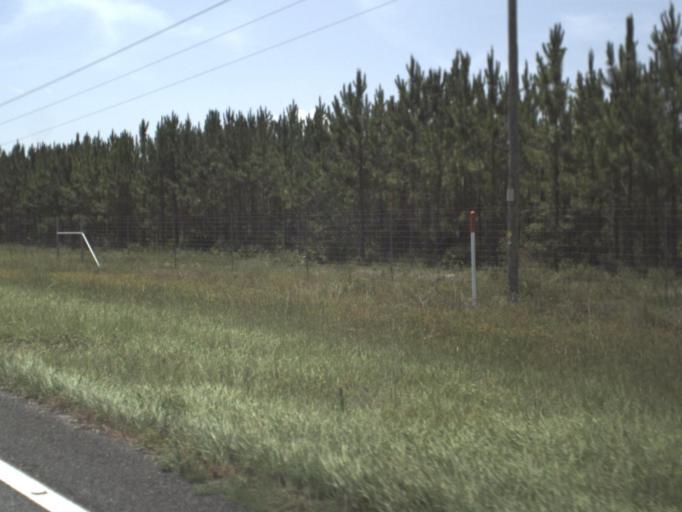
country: US
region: Florida
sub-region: Taylor County
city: Steinhatchee
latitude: 29.7887
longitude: -83.3322
